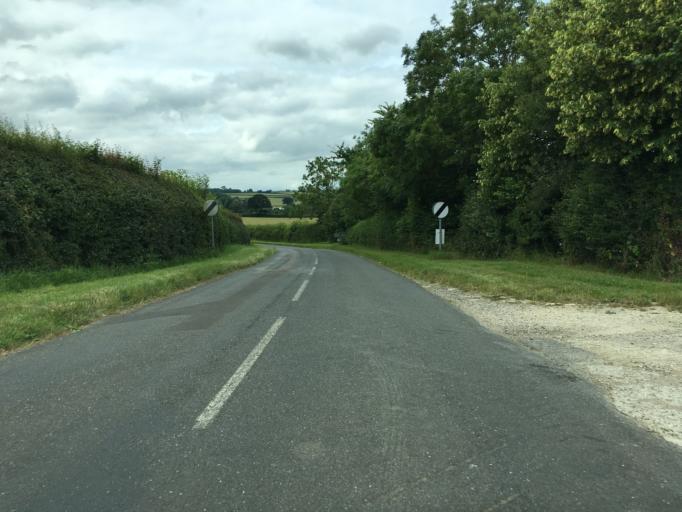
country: GB
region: England
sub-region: Oxfordshire
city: Shipton under Wychwood
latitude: 51.8927
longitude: -1.6425
